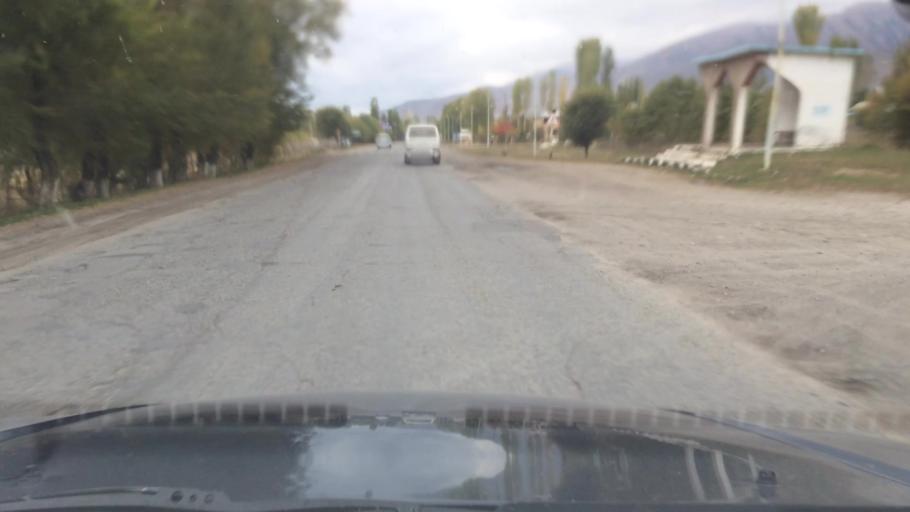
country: KG
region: Ysyk-Koel
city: Tyup
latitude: 42.7849
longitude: 78.2468
